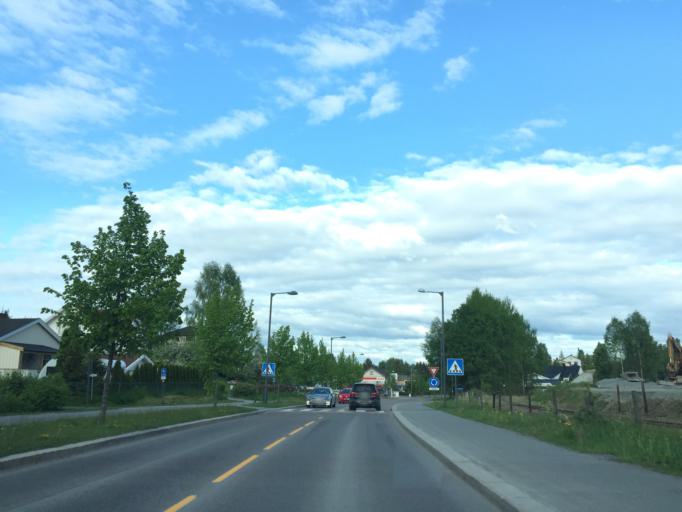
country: NO
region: Akershus
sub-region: Sorum
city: Sorumsand
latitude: 59.9869
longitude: 11.2471
